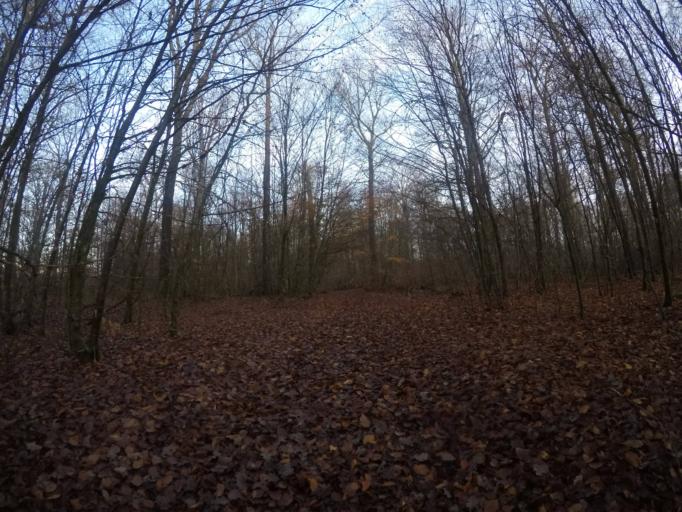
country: BE
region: Wallonia
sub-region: Province du Luxembourg
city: Habay-la-Vieille
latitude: 49.7455
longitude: 5.6731
